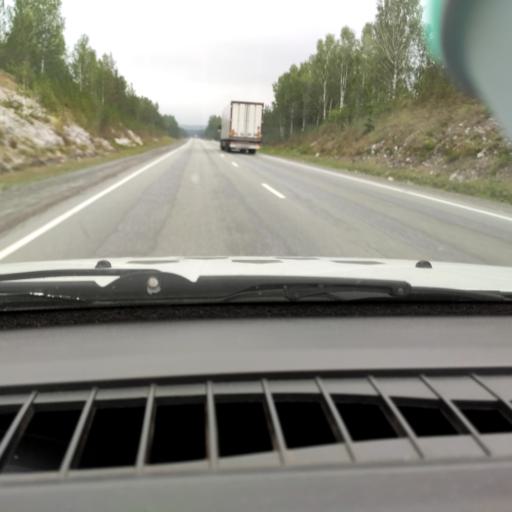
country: RU
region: Chelyabinsk
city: Syrostan
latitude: 55.0055
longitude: 59.8142
